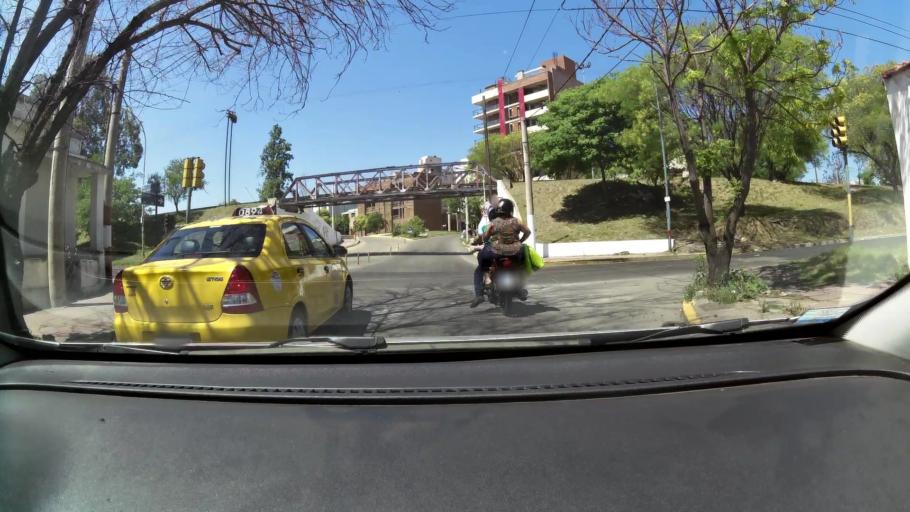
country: AR
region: Cordoba
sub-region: Departamento de Capital
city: Cordoba
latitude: -31.3990
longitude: -64.1935
